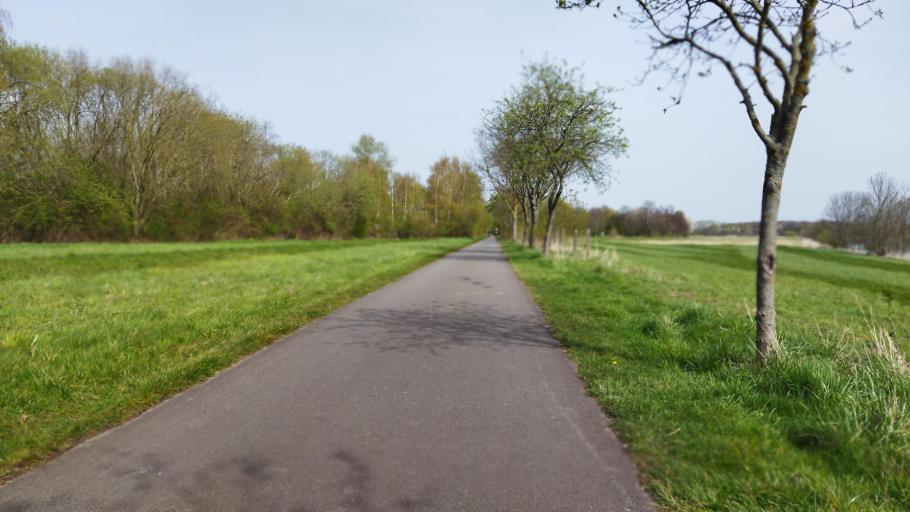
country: DE
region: North Rhine-Westphalia
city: Porta Westfalica
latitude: 52.2616
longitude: 8.9192
